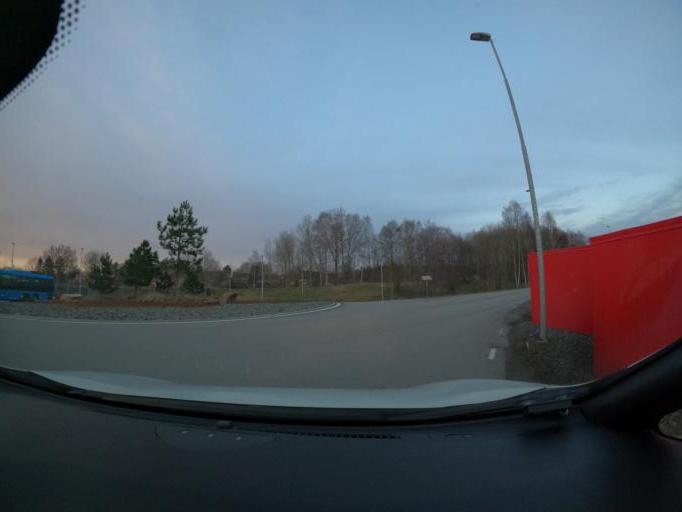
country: SE
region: Vaestra Goetaland
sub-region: Harryda Kommun
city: Molnlycke
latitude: 57.6543
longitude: 12.1292
